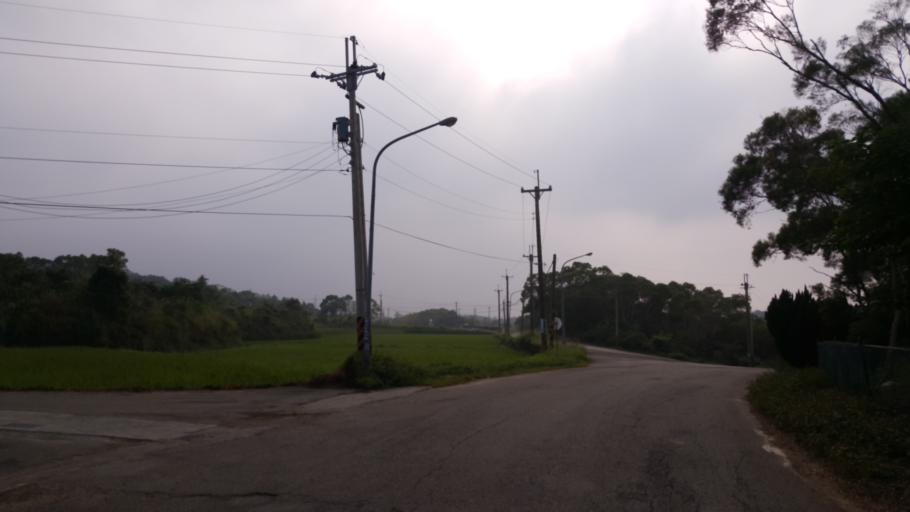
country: TW
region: Taiwan
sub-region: Hsinchu
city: Hsinchu
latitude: 24.7109
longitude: 120.9483
